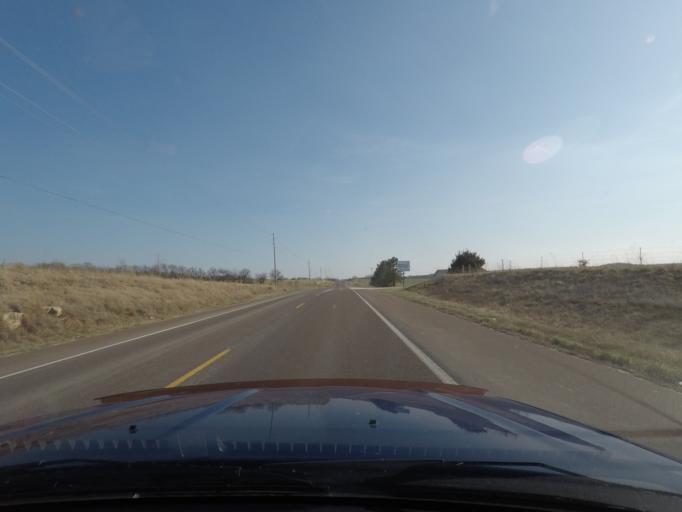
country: US
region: Kansas
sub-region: Douglas County
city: Lawrence
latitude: 39.0245
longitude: -95.3914
